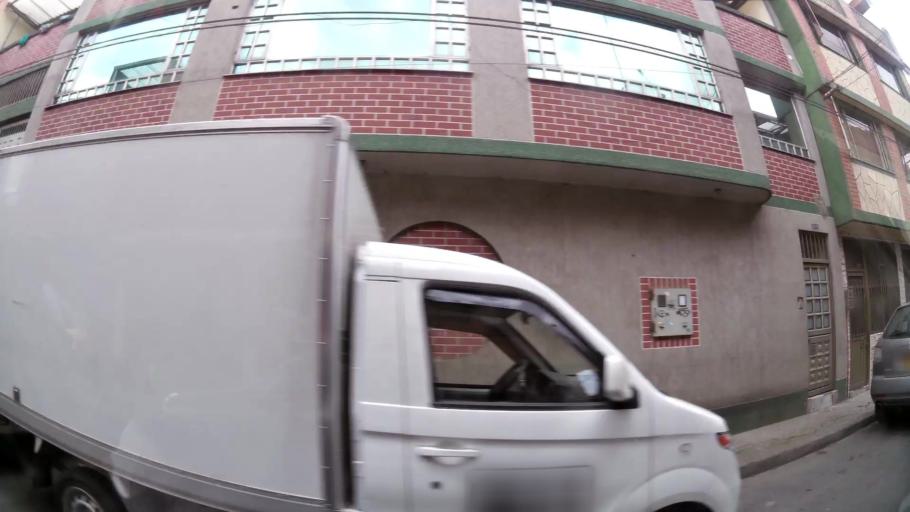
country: CO
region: Cundinamarca
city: Funza
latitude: 4.7041
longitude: -74.1302
